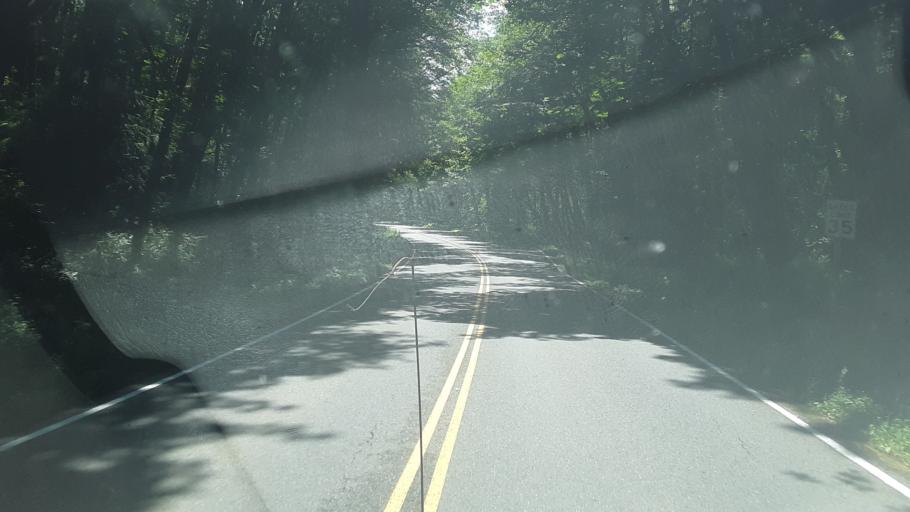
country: US
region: Washington
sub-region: Clark County
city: Yacolt
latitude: 46.0745
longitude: -122.2073
